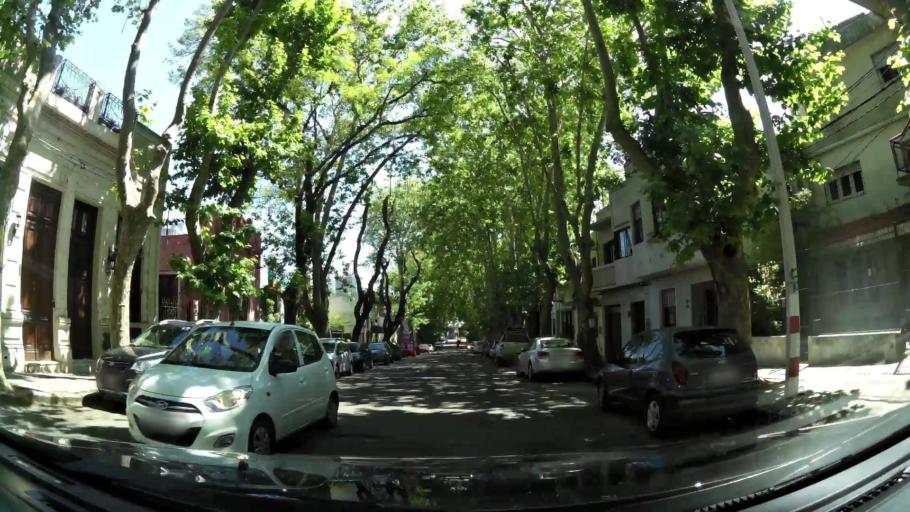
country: UY
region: Montevideo
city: Montevideo
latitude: -34.9174
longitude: -56.1596
